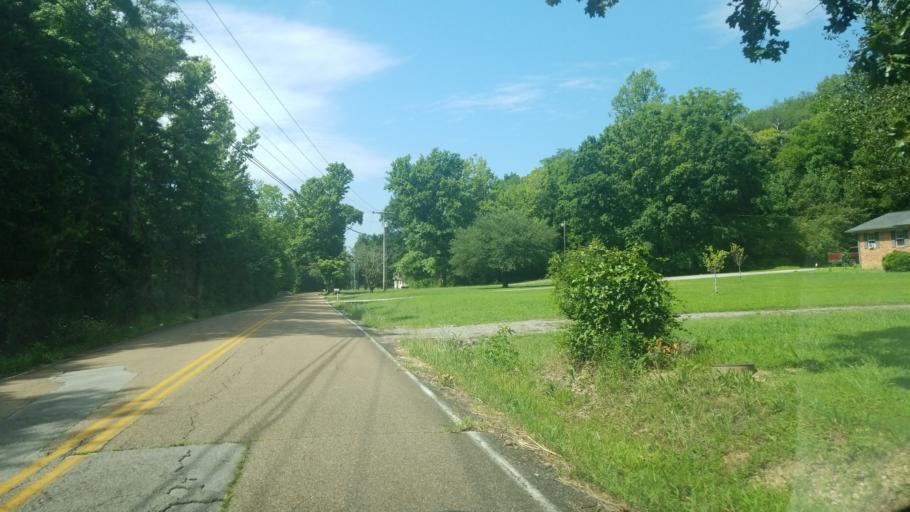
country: US
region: Tennessee
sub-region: Hamilton County
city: Lakesite
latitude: 35.1723
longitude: -85.0631
